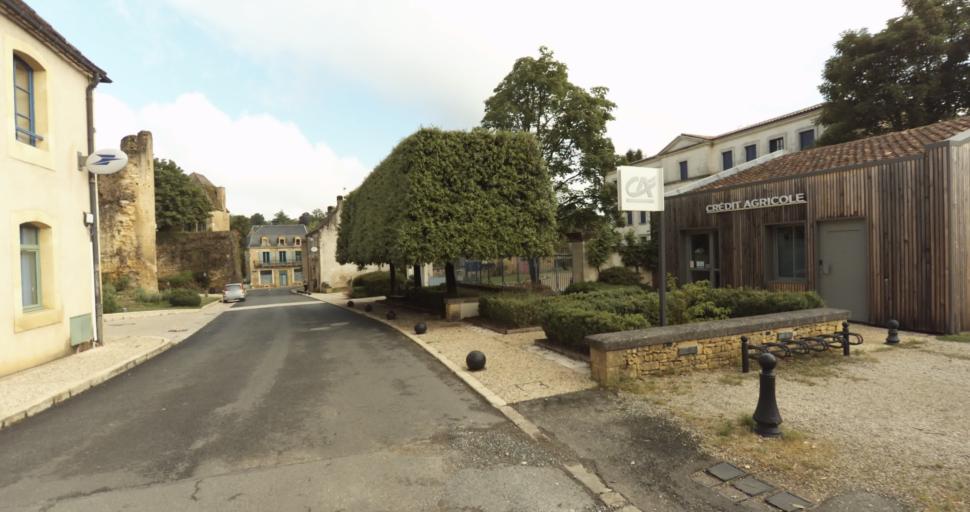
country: FR
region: Aquitaine
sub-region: Departement de la Dordogne
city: Le Bugue
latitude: 44.9464
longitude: 0.8096
